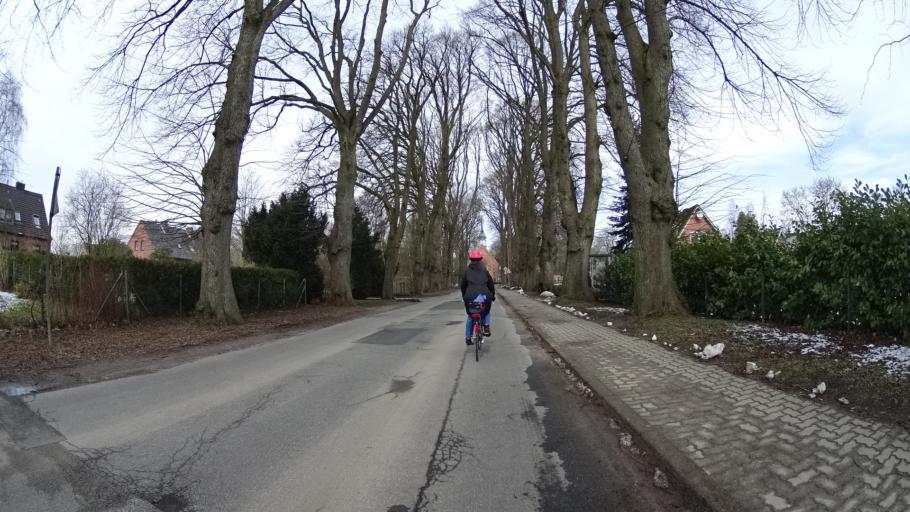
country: DE
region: Schleswig-Holstein
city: Rendswuhren
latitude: 54.0815
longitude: 10.1958
